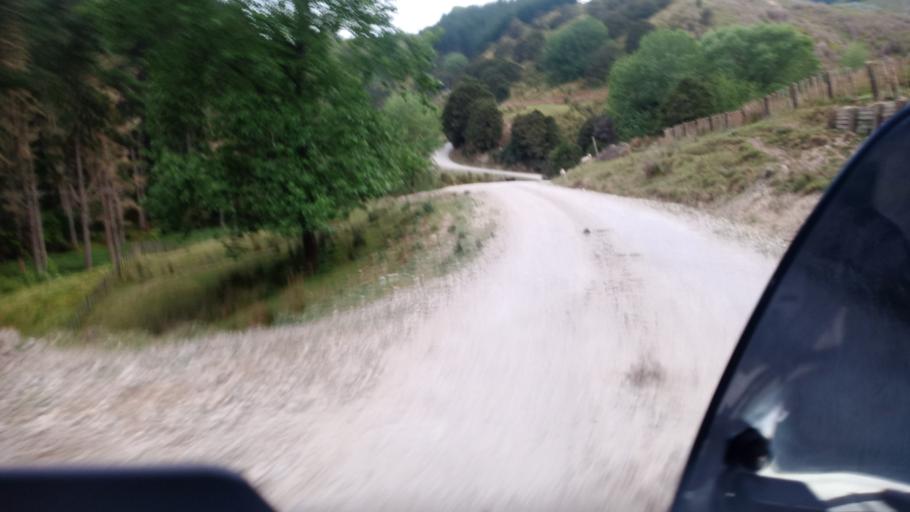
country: NZ
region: Gisborne
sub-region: Gisborne District
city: Gisborne
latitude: -38.4807
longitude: 177.9639
